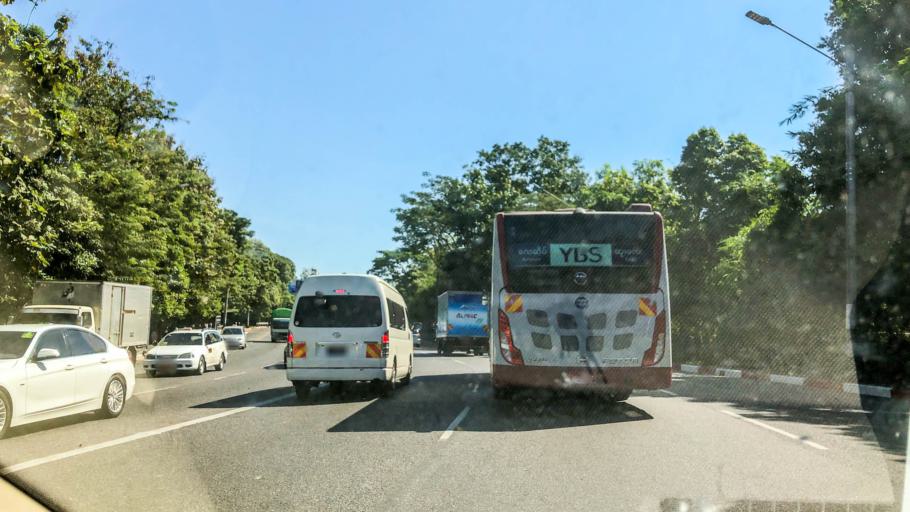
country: MM
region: Yangon
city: Yangon
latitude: 16.8877
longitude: 96.1339
